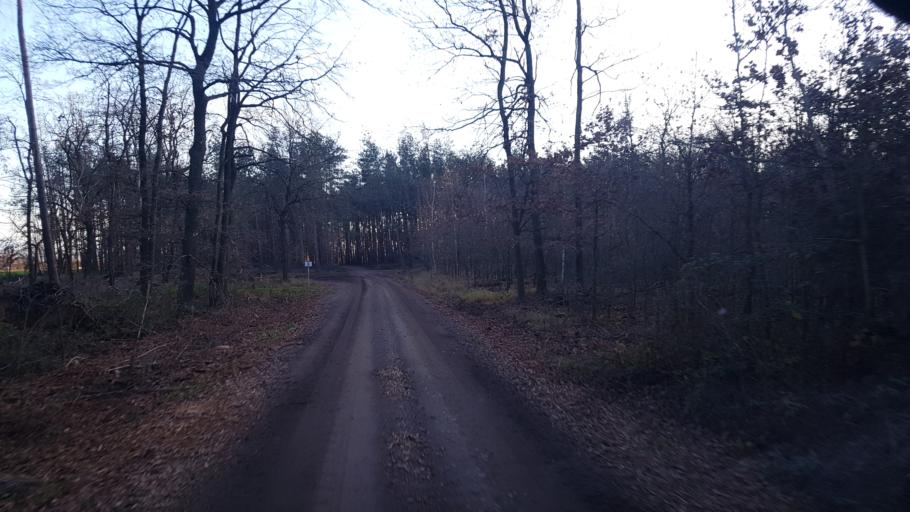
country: DE
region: Brandenburg
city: Falkenberg
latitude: 51.6153
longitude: 13.2823
